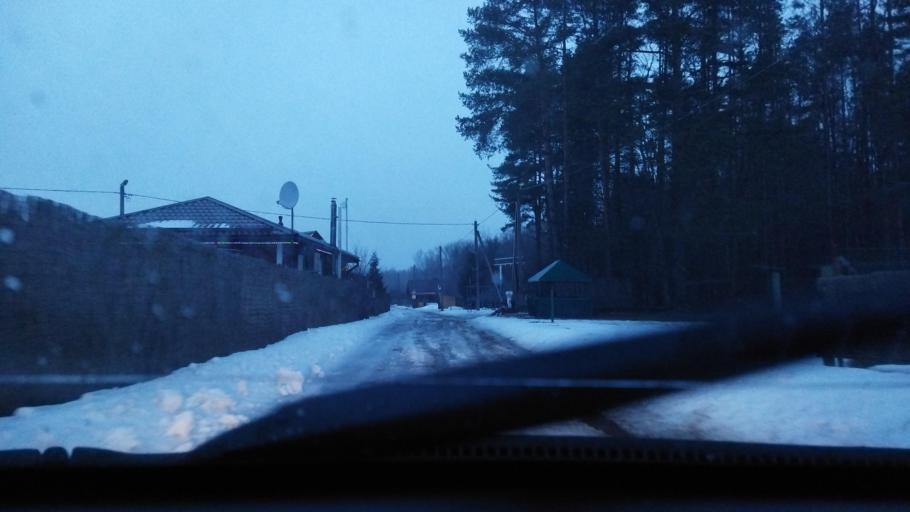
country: BY
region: Minsk
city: Svir
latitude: 54.9402
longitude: 26.4050
